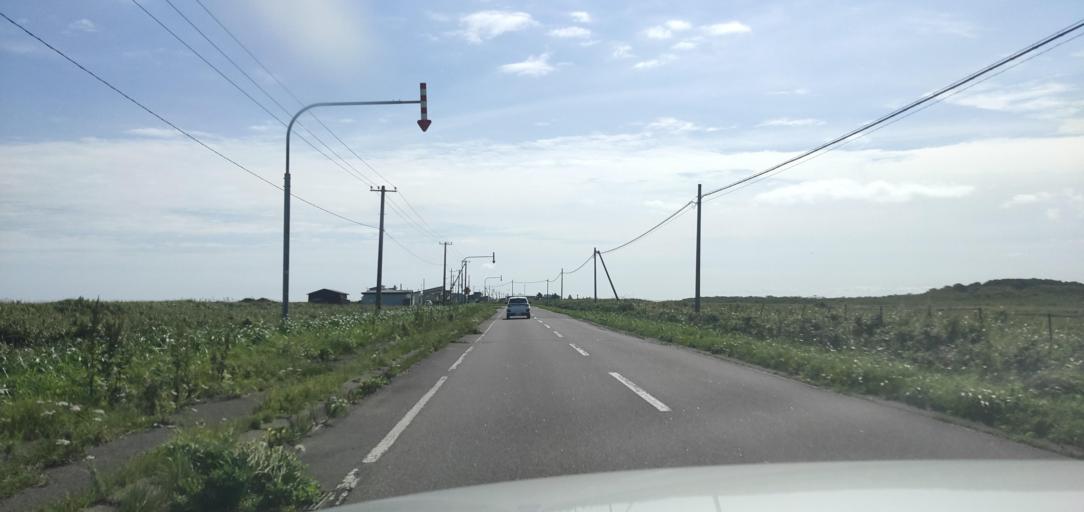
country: JP
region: Hokkaido
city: Shibetsu
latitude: 43.6331
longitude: 145.1815
